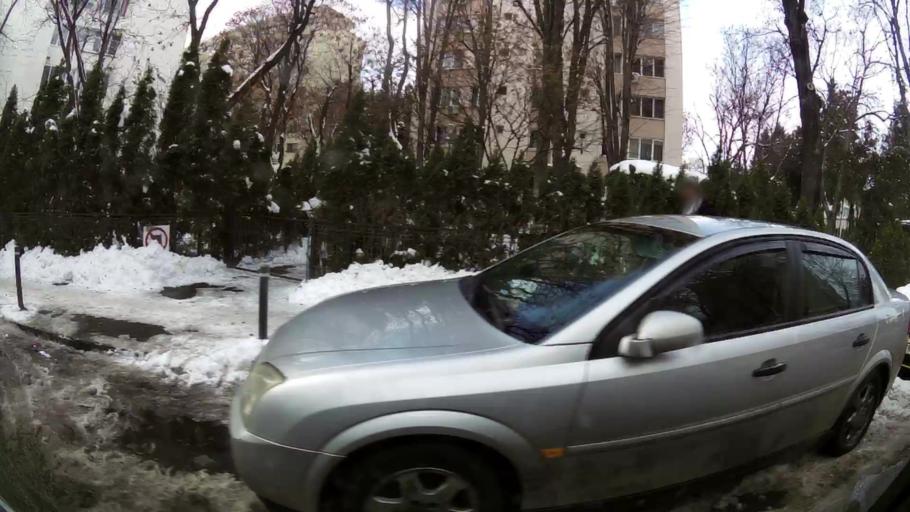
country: RO
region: Ilfov
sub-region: Comuna Popesti-Leordeni
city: Popesti-Leordeni
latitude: 44.3831
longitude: 26.1197
